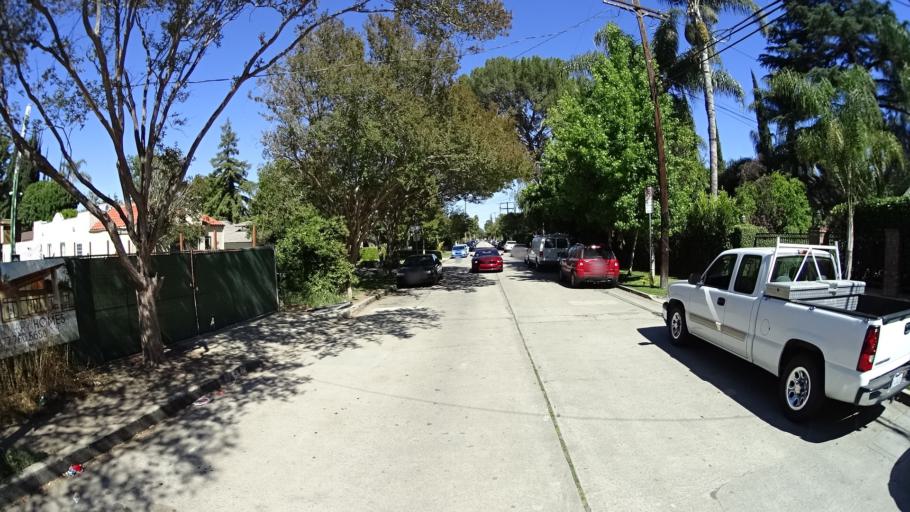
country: US
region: California
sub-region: Los Angeles County
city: Sherman Oaks
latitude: 34.1510
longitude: -118.4657
